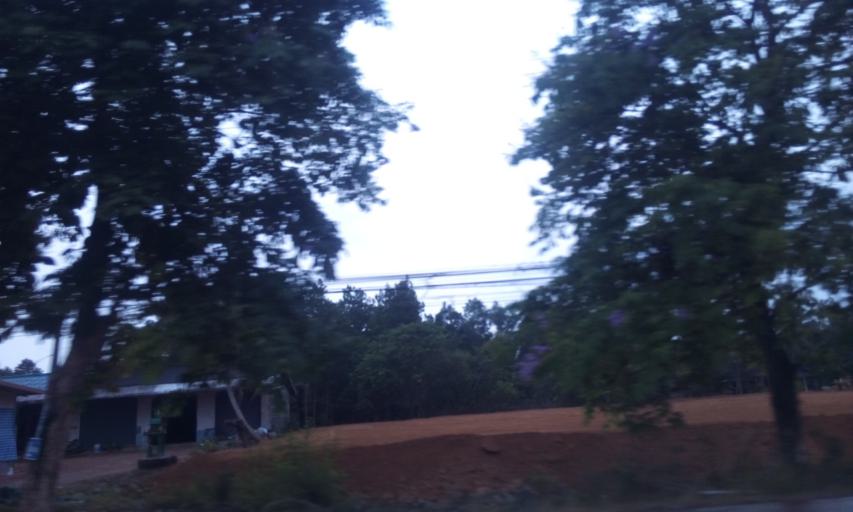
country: TH
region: Trat
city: Khao Saming
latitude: 12.4019
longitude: 102.3445
